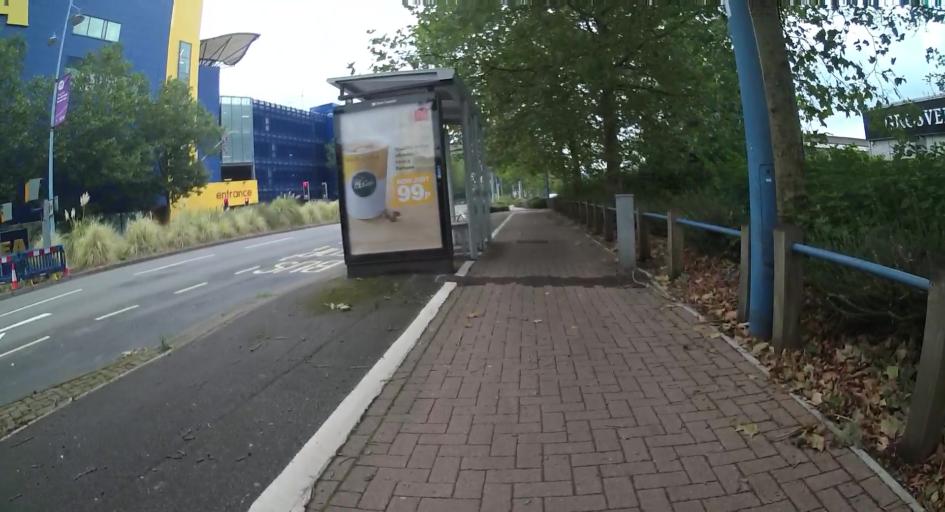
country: GB
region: England
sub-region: Southampton
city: Southampton
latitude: 50.9029
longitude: -1.4121
